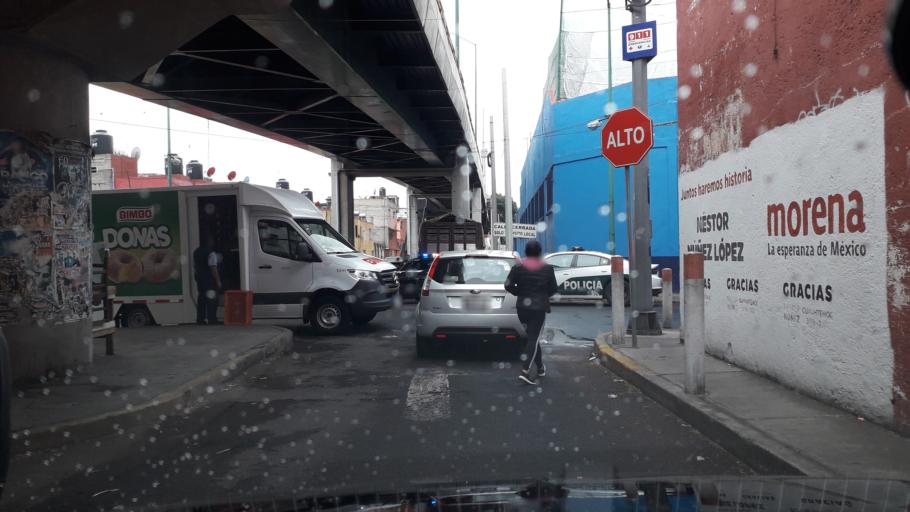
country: MX
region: Mexico City
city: Cuauhtemoc
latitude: 19.4596
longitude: -99.1543
